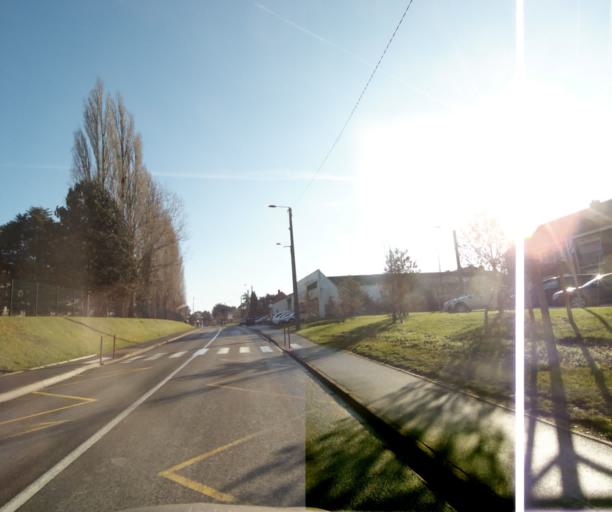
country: FR
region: Nord-Pas-de-Calais
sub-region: Departement du Nord
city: Marly
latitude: 50.3433
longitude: 3.5467
